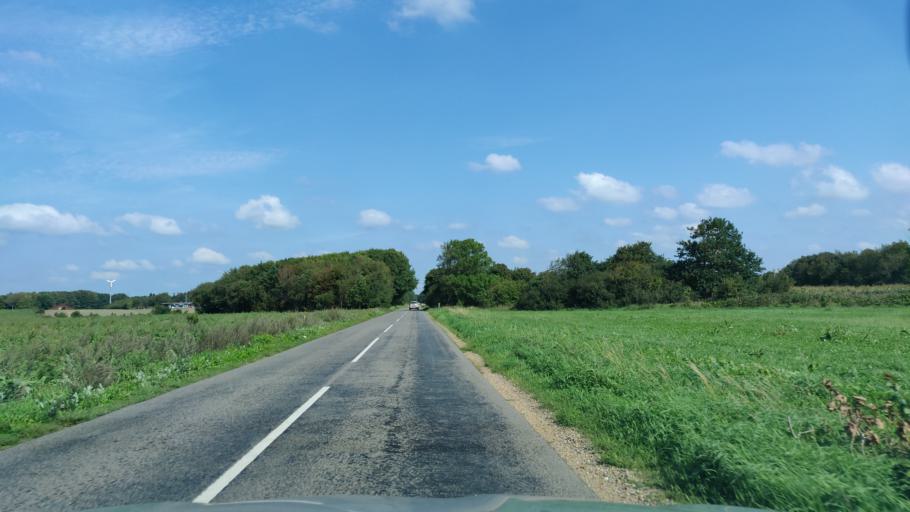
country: DK
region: Central Jutland
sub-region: Herning Kommune
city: Avlum
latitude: 56.2250
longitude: 8.8615
